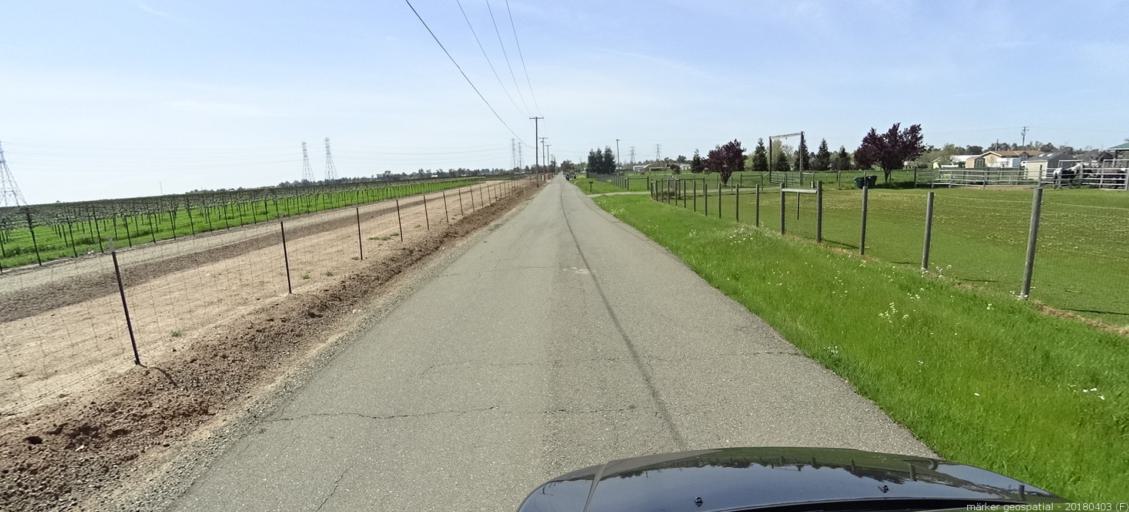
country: US
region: California
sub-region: Sacramento County
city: Clay
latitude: 38.3504
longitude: -121.1946
